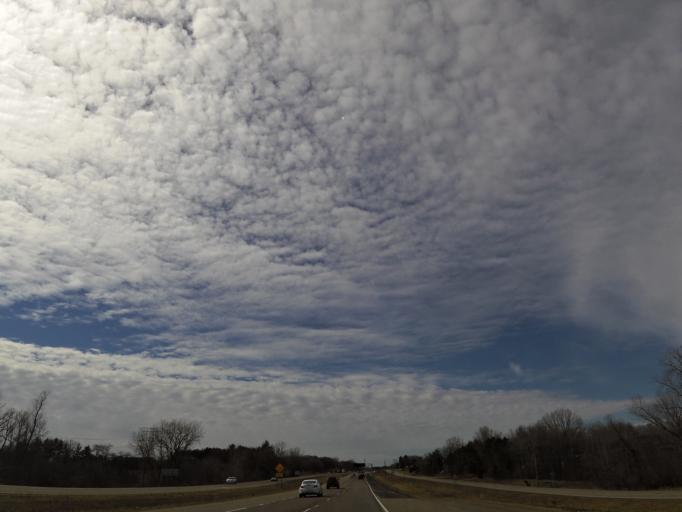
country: US
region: Minnesota
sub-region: Washington County
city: Mahtomedi
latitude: 45.0357
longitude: -92.9299
